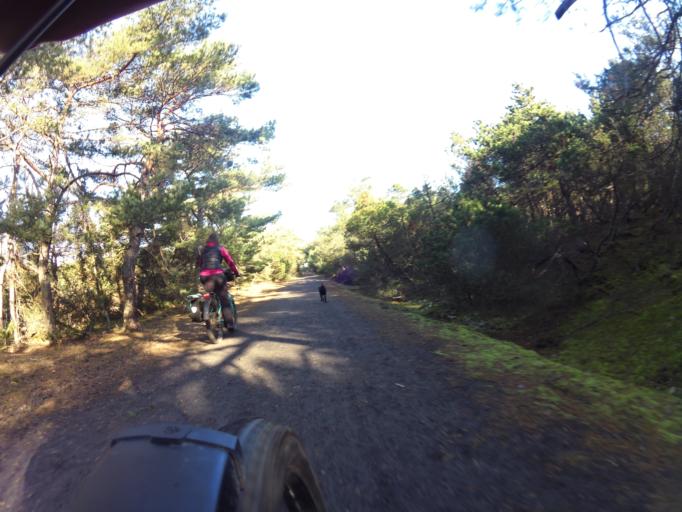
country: PL
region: Pomeranian Voivodeship
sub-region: Powiat pucki
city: Hel
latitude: 54.6036
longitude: 18.8176
